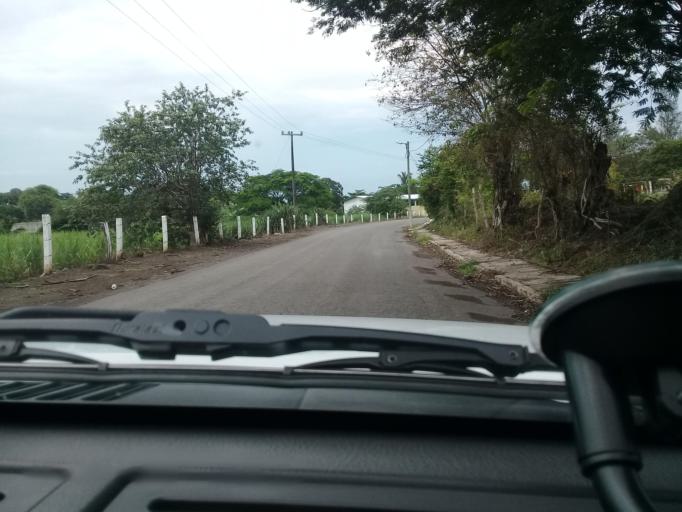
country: MX
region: Veracruz
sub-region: Paso de Ovejas
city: El Hatito
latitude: 19.3109
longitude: -96.3720
